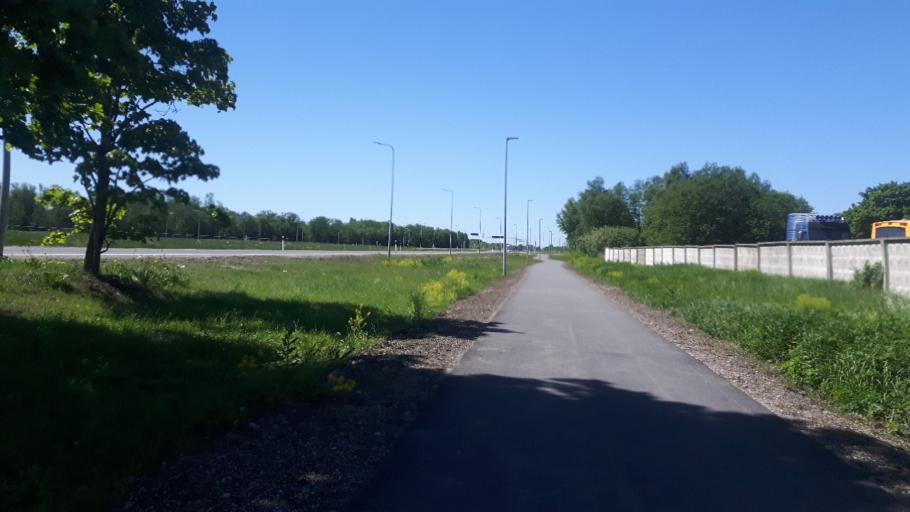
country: EE
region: Ida-Virumaa
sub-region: Sillamaee linn
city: Sillamae
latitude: 59.3914
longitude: 27.7452
